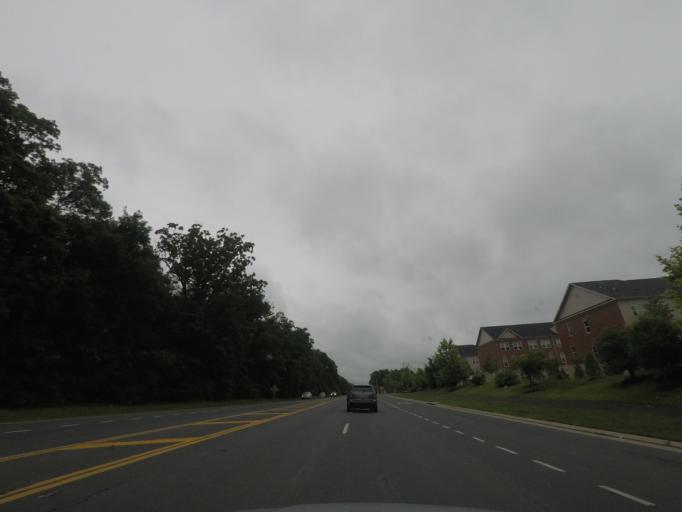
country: US
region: Virginia
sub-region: Prince William County
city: Haymarket
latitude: 38.7858
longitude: -77.6662
